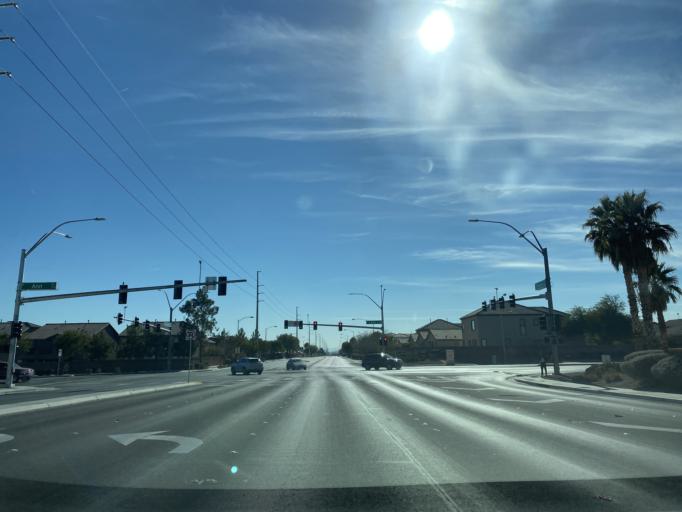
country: US
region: Nevada
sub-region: Clark County
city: North Las Vegas
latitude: 36.2621
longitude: -115.1440
